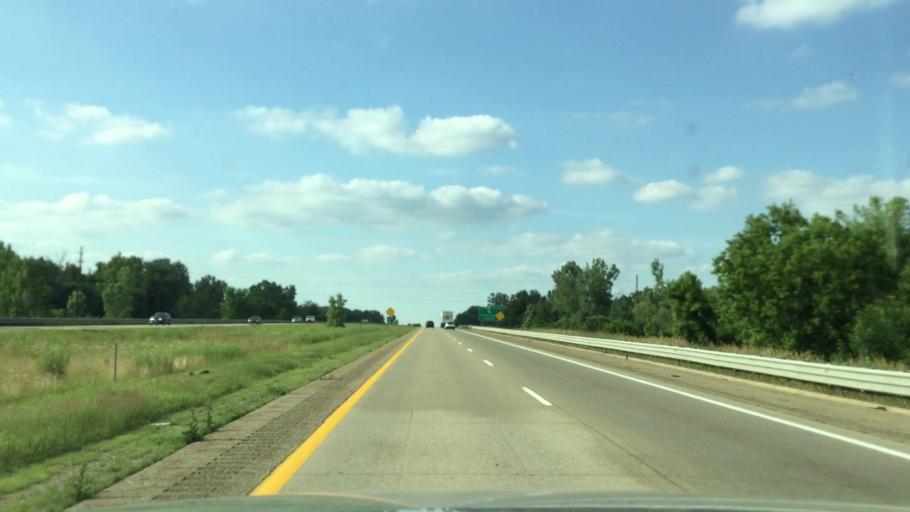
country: US
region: Michigan
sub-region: Branch County
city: Union City
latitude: 42.0967
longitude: -84.9969
